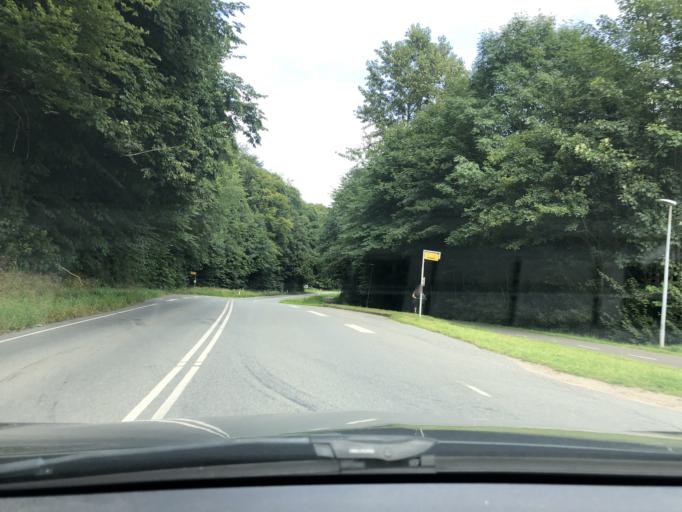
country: DK
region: South Denmark
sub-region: Vejle Kommune
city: Vejle
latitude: 55.6939
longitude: 9.4842
